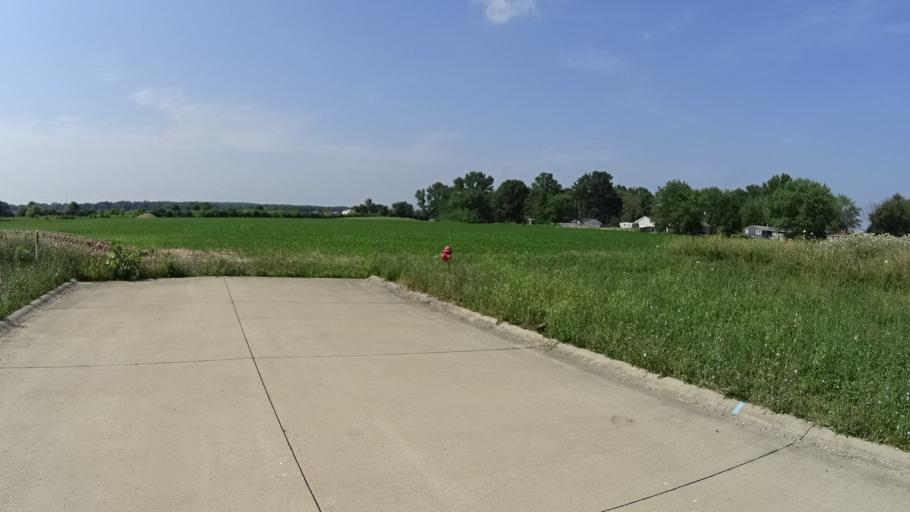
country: US
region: Ohio
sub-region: Lorain County
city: Vermilion
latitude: 41.4140
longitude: -82.3748
